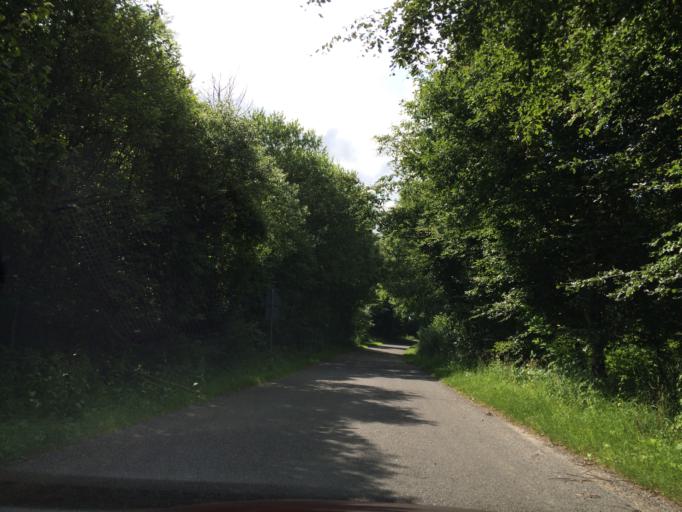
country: DK
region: Central Jutland
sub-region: Skanderborg Kommune
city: Galten
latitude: 56.1626
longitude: 9.8534
